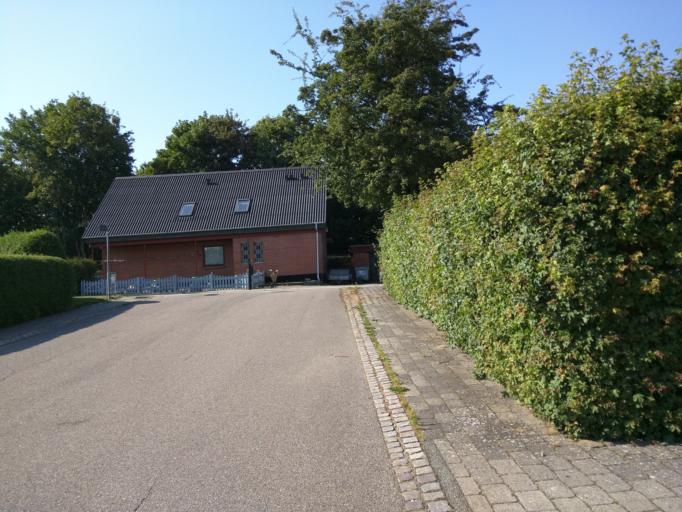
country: DK
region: Central Jutland
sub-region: Viborg Kommune
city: Viborg
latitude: 56.4335
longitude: 9.3977
